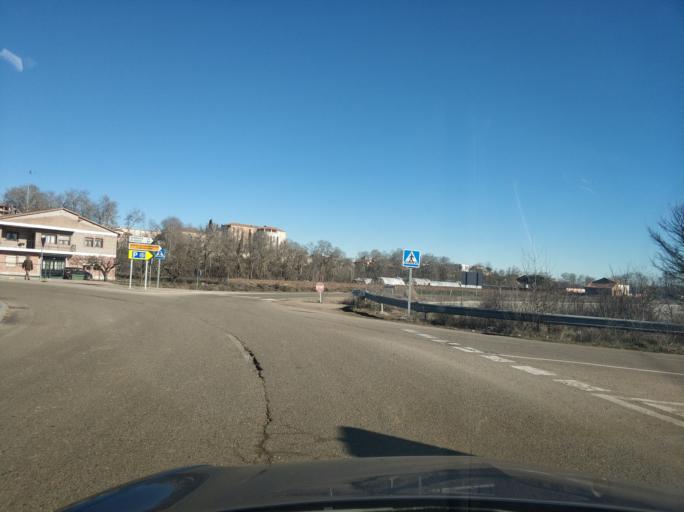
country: ES
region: Castille and Leon
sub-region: Provincia de Valladolid
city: Tordesillas
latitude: 41.4964
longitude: -5.0002
